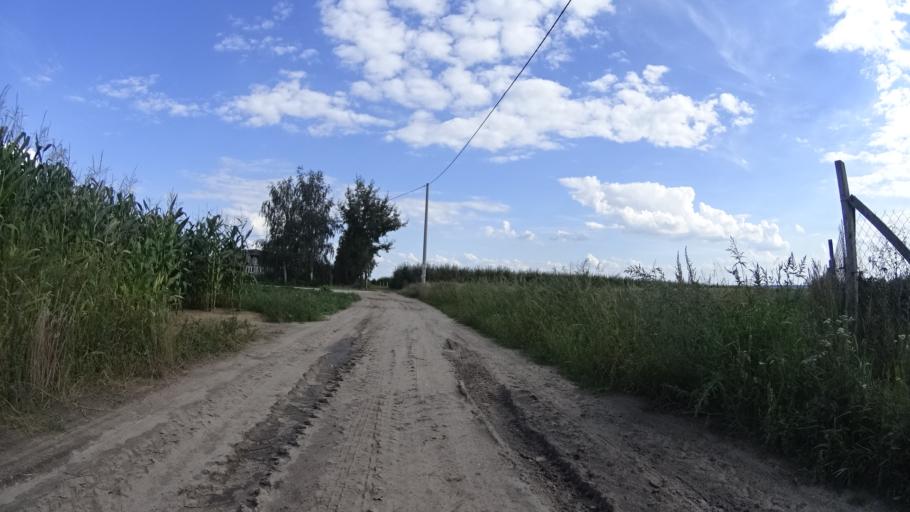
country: PL
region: Masovian Voivodeship
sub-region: Powiat bialobrzeski
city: Wysmierzyce
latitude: 51.6696
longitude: 20.8051
